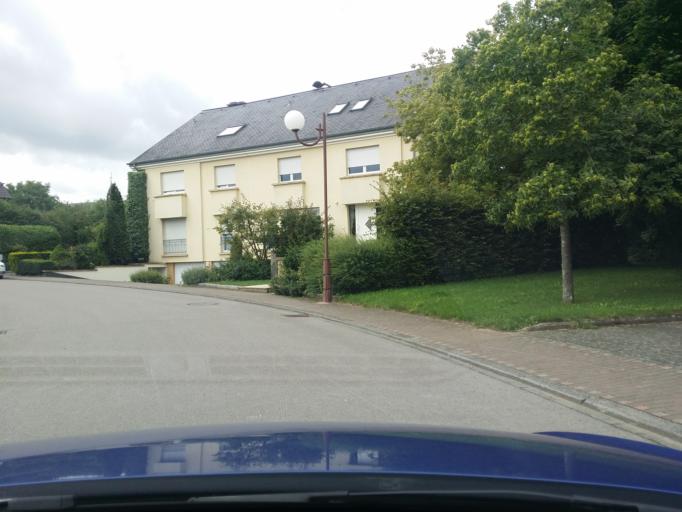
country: LU
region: Luxembourg
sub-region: Canton de Luxembourg
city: Bertrange
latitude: 49.6084
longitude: 6.0527
